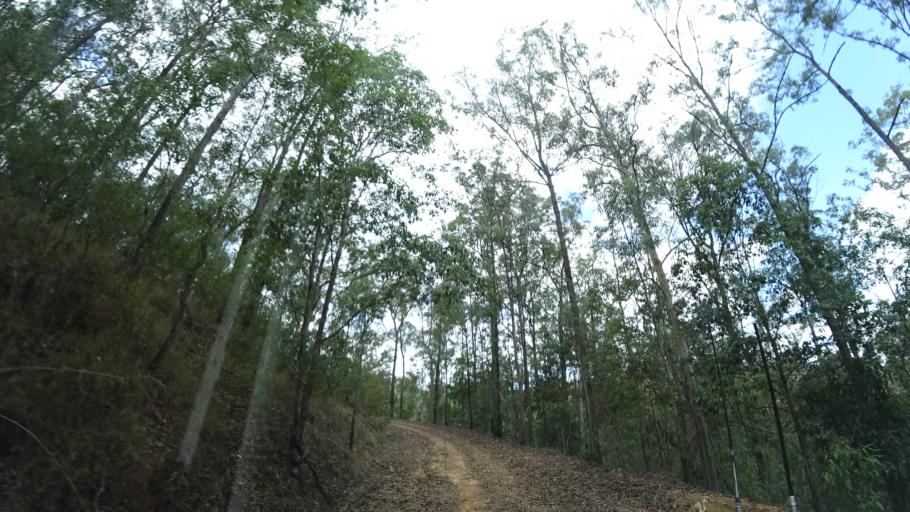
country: AU
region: Queensland
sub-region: Moreton Bay
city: Highvale
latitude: -27.3671
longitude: 152.7349
